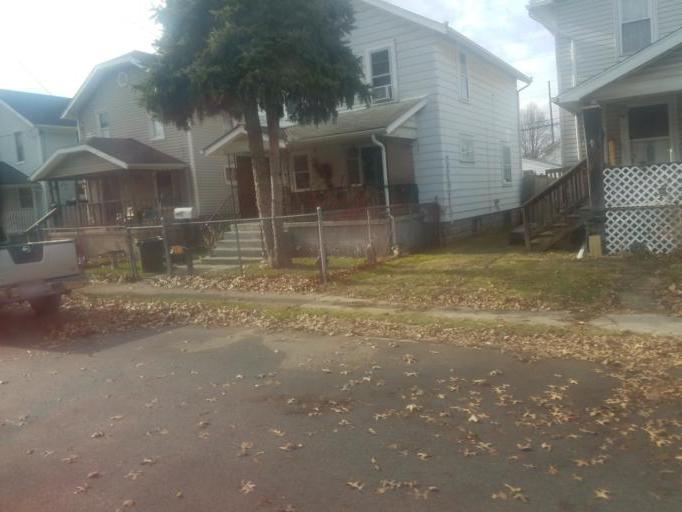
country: US
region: Ohio
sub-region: Marion County
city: Marion
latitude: 40.5775
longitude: -83.1445
